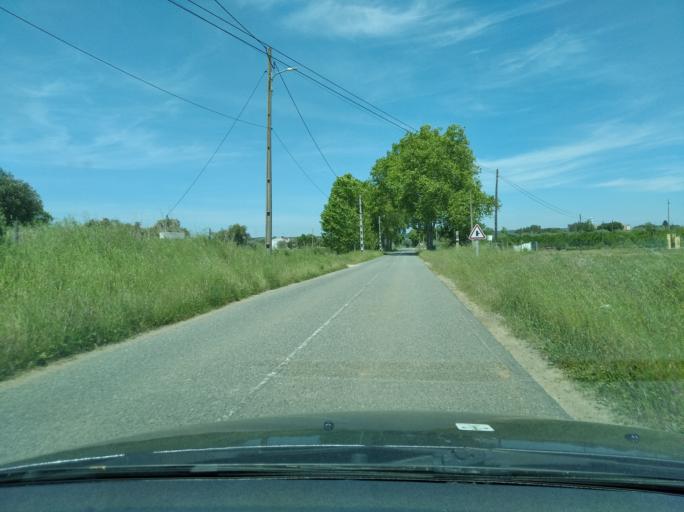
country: PT
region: Portalegre
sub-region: Avis
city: Avis
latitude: 39.0973
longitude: -7.8788
